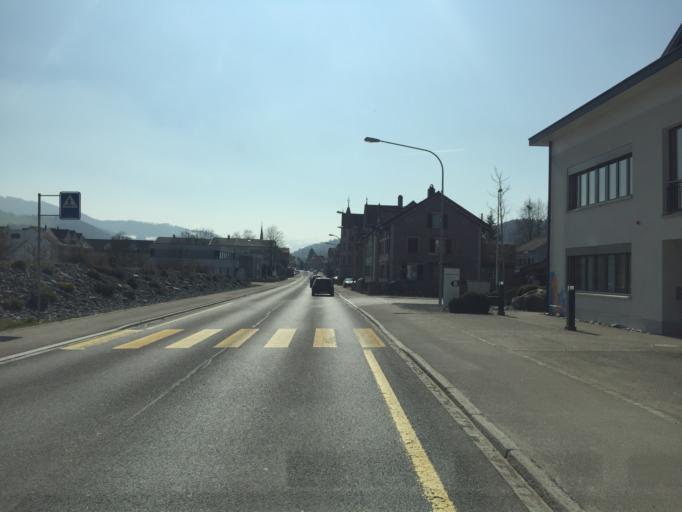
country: CH
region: Saint Gallen
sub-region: Wahlkreis Toggenburg
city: Buetschwil
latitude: 47.3576
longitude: 9.0732
